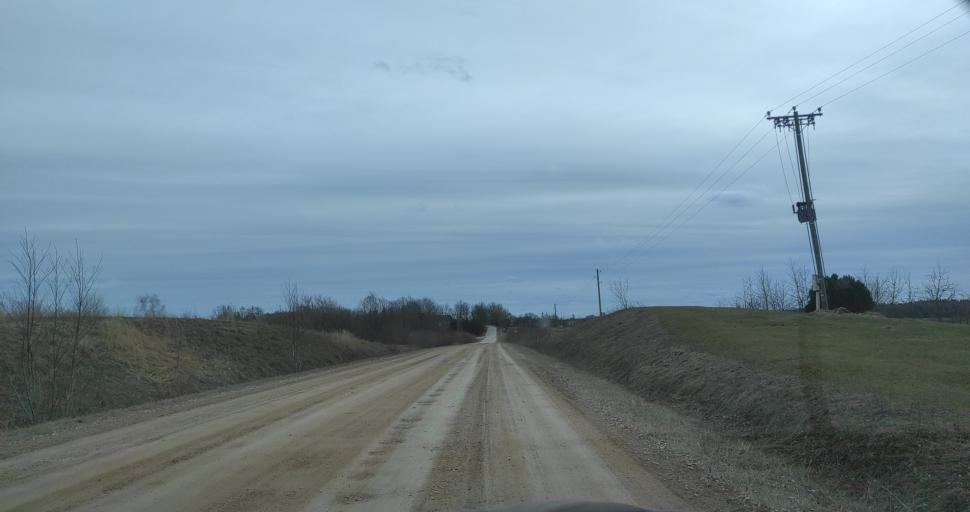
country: LV
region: Tukuma Rajons
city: Tukums
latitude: 57.0634
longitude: 23.0233
